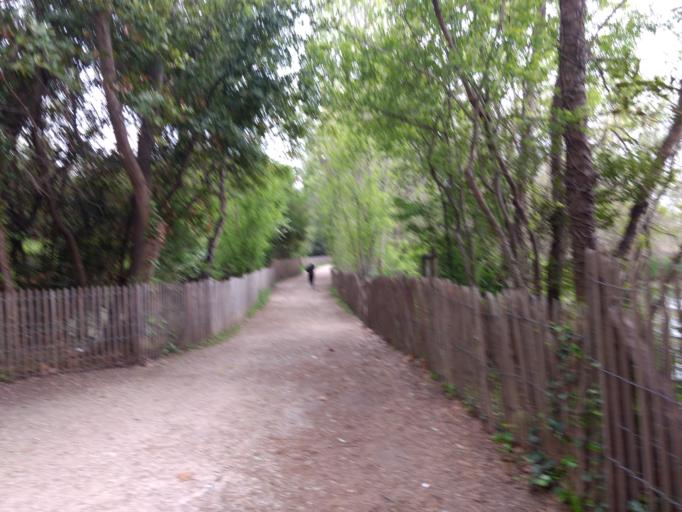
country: FR
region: Provence-Alpes-Cote d'Azur
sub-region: Departement des Alpes-Maritimes
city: Biot
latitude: 43.6219
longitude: 7.1290
